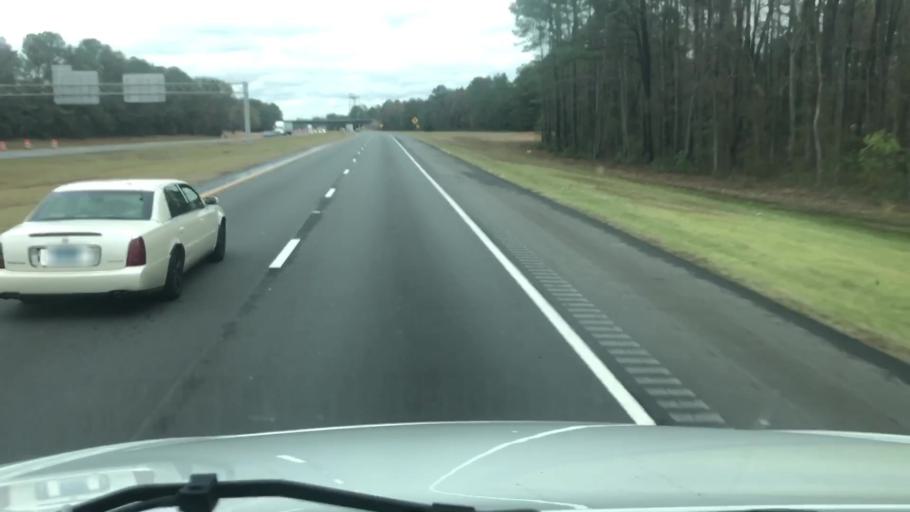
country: US
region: North Carolina
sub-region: Cumberland County
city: Eastover
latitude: 35.0909
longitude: -78.7810
